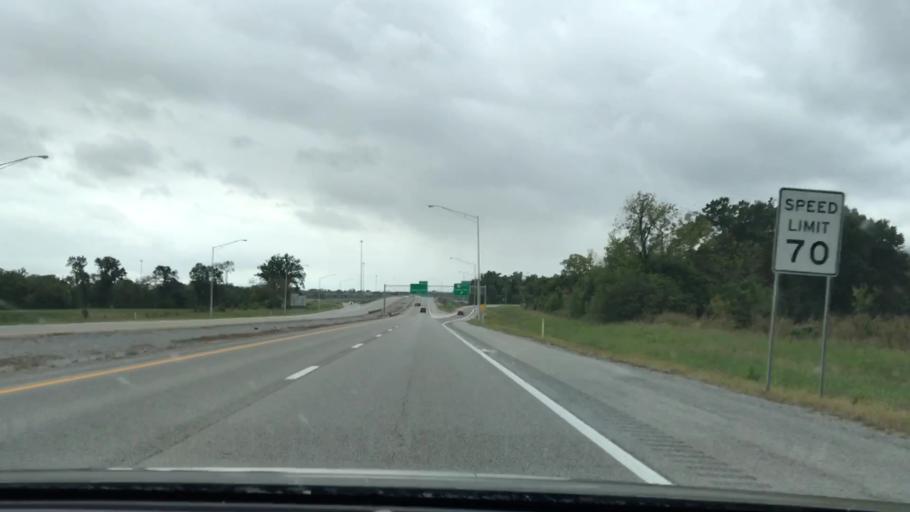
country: US
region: Kentucky
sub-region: Christian County
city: Hopkinsville
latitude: 36.8244
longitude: -87.4790
